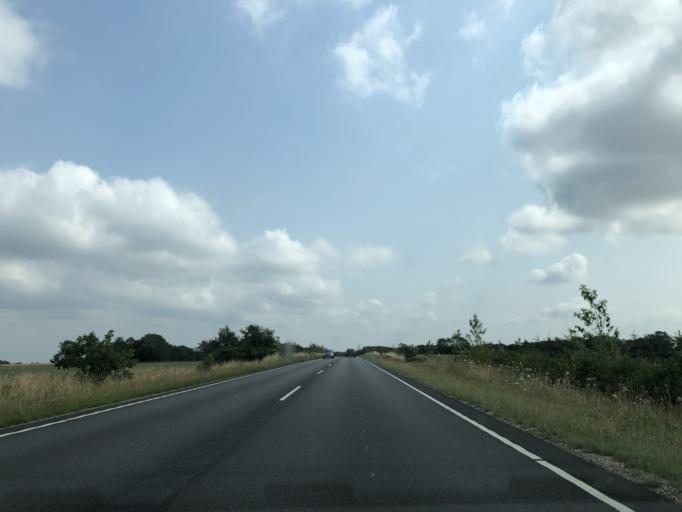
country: DK
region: Central Jutland
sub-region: Viborg Kommune
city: Bjerringbro
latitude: 56.3308
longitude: 9.5489
